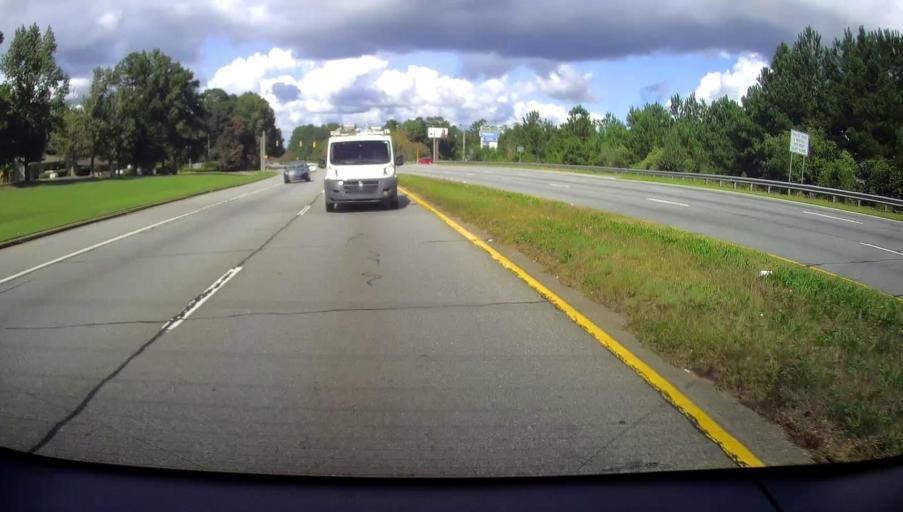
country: US
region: Georgia
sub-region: Bibb County
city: Macon
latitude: 32.8643
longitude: -83.6127
